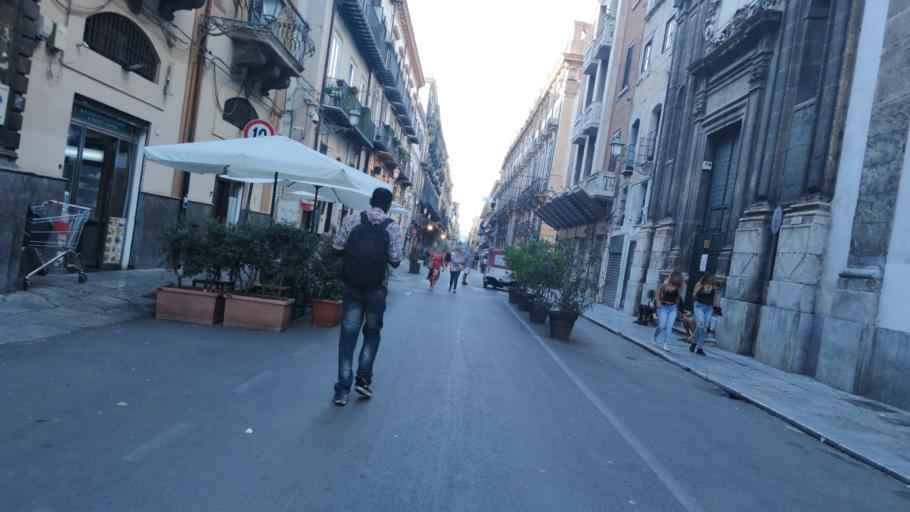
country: IT
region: Sicily
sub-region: Palermo
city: Palermo
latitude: 38.1115
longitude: 13.3642
